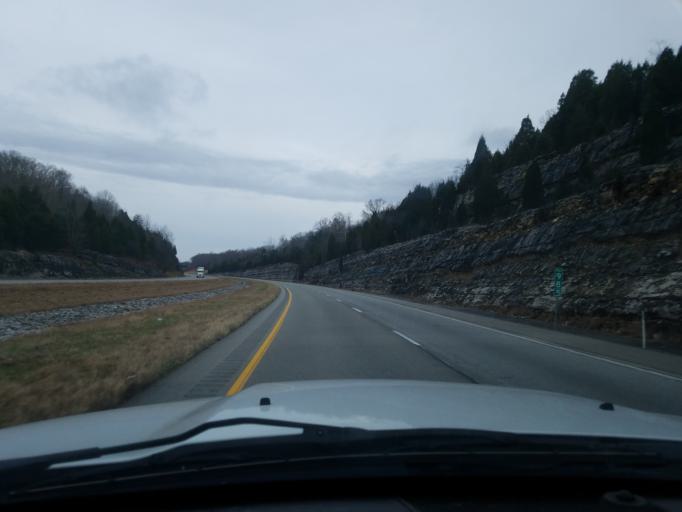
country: US
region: Indiana
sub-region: Harrison County
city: Corydon
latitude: 38.2380
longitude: -86.2441
